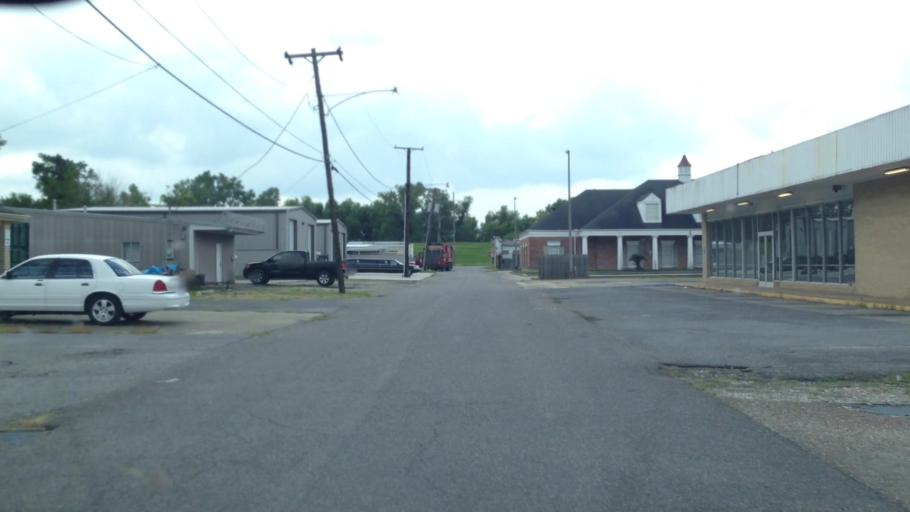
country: US
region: Louisiana
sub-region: Saint Charles Parish
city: Norco
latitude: 29.9982
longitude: -90.4125
